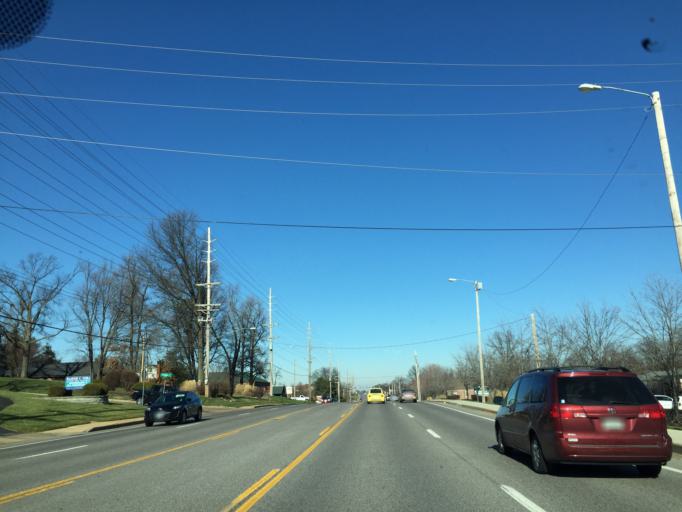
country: US
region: Missouri
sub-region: Saint Louis County
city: Ellisville
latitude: 38.5986
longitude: -90.5857
